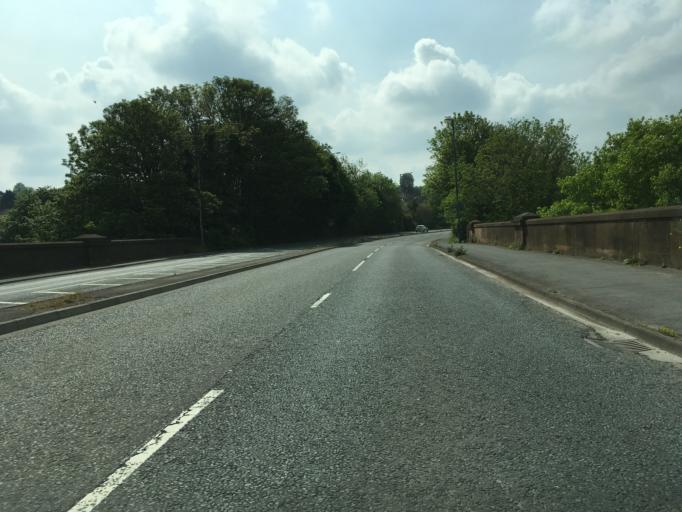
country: GB
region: England
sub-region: North Somerset
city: Easton-in-Gordano
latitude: 51.4808
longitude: -2.6486
